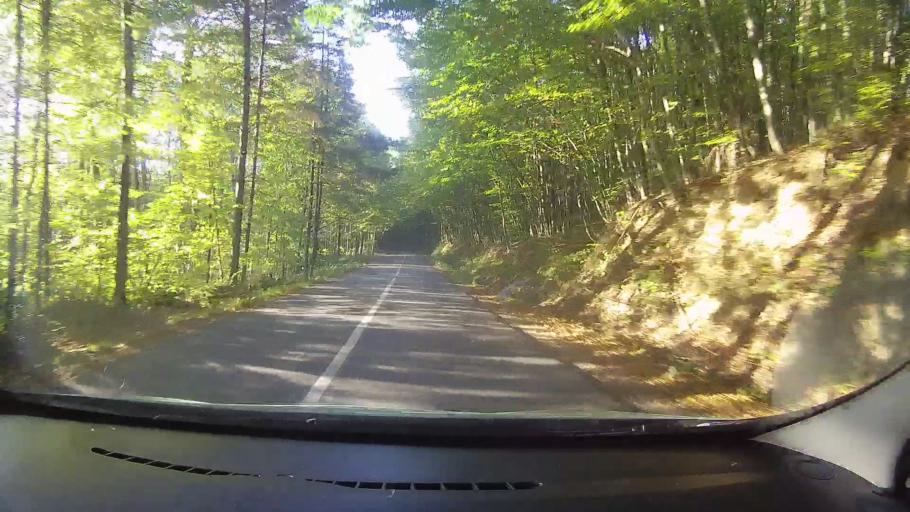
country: RO
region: Timis
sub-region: Comuna Nadrag
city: Nadrag
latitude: 45.6747
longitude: 22.1637
